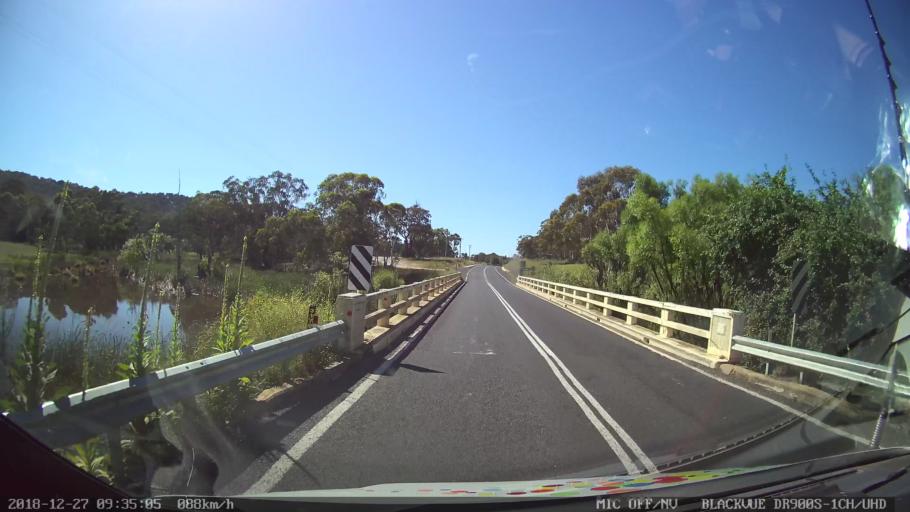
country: AU
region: New South Wales
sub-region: Lithgow
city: Portland
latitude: -33.2344
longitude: 150.0276
